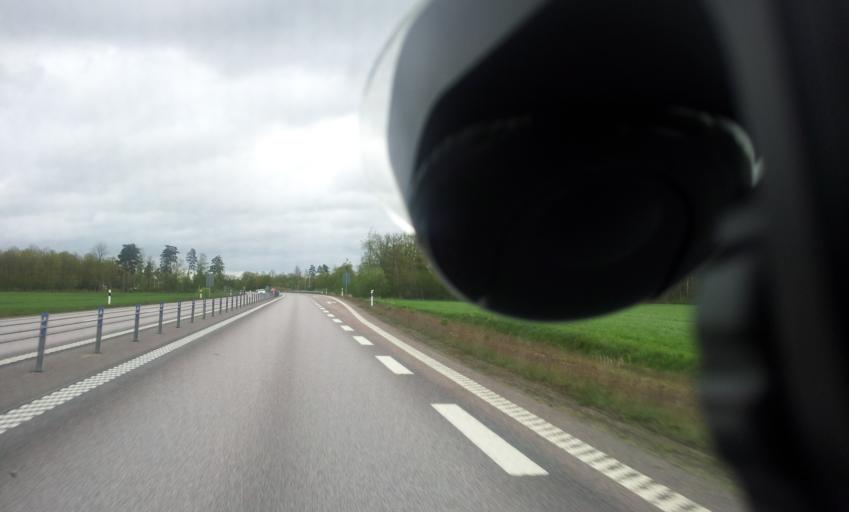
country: SE
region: Kalmar
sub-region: Kalmar Kommun
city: Ljungbyholm
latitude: 56.5765
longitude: 16.1086
